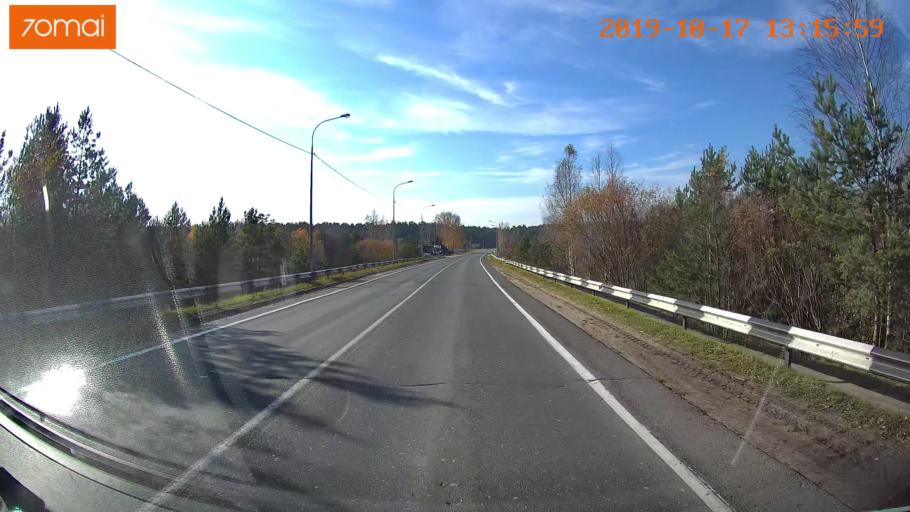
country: RU
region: Rjazan
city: Gus'-Zheleznyy
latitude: 55.0502
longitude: 41.1481
